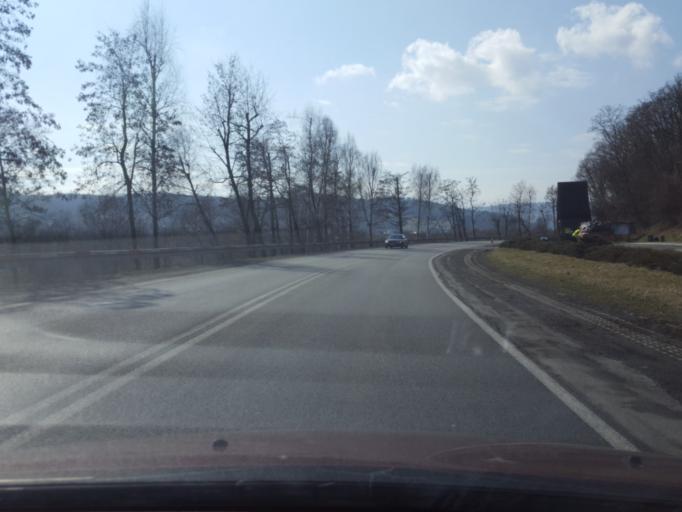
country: PL
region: Lesser Poland Voivodeship
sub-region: Powiat nowosadecki
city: Lososina Dolna
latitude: 49.6968
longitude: 20.6604
